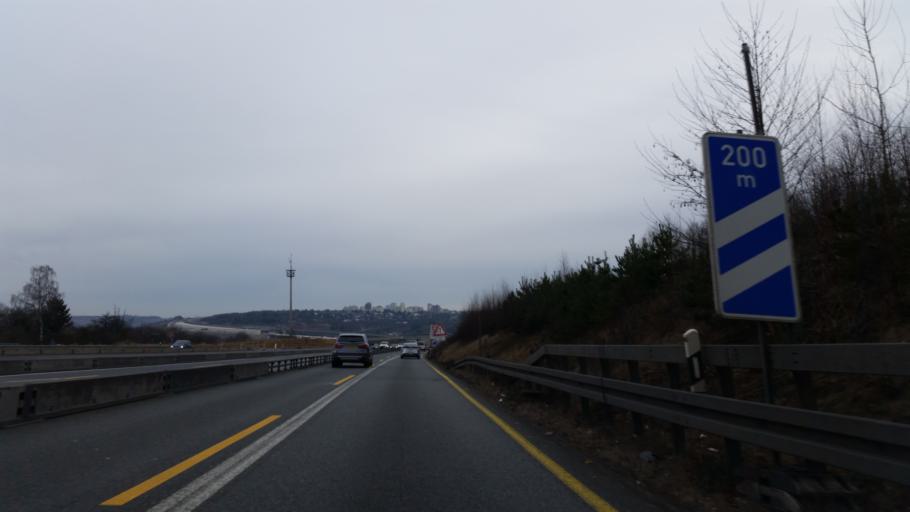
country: DE
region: Bavaria
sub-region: Regierungsbezirk Unterfranken
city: Reichenberg
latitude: 49.7558
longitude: 9.9176
